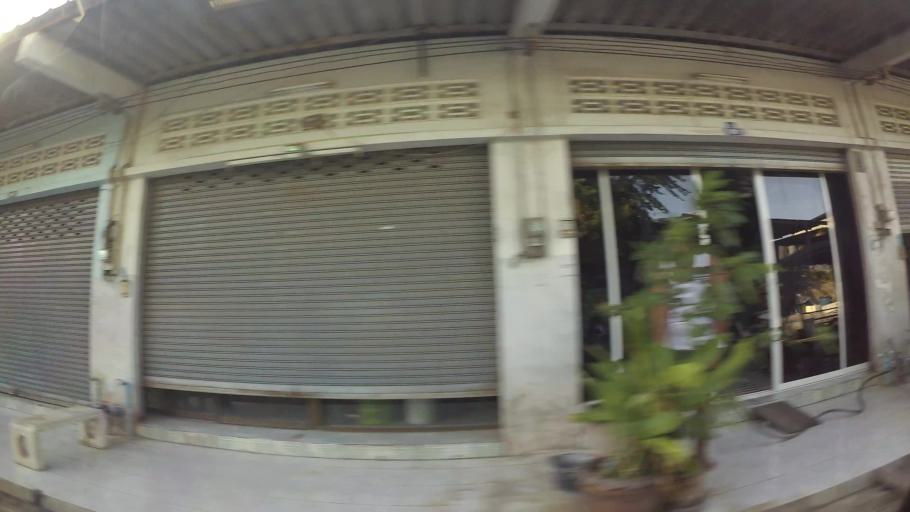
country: TH
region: Rayong
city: Rayong
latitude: 12.6902
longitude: 101.2745
